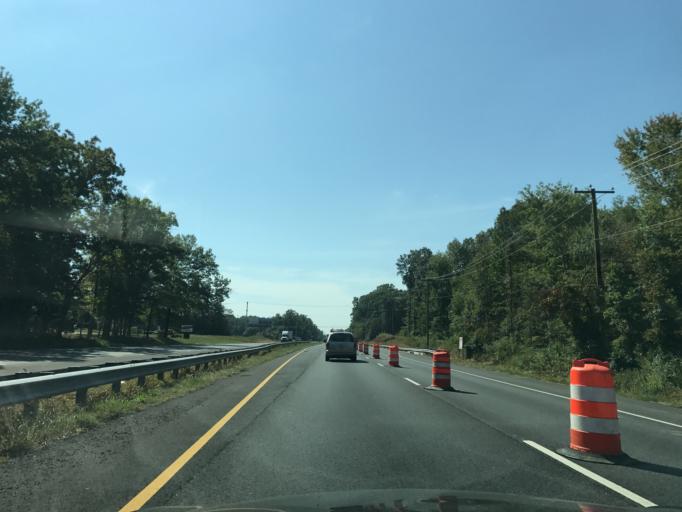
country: US
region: Maryland
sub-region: Cecil County
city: North East
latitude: 39.6036
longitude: -75.9613
